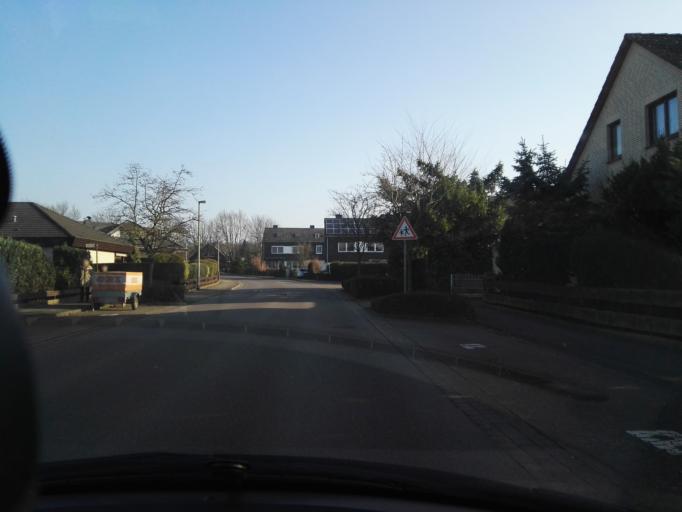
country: DE
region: Lower Saxony
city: Sarstedt
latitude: 52.2436
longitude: 9.8598
